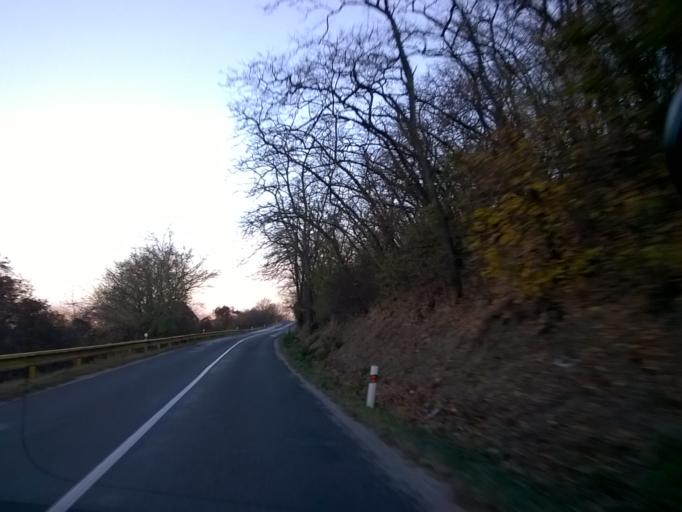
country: SK
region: Nitriansky
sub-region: Okres Nitra
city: Nitra
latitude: 48.3795
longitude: 18.0920
